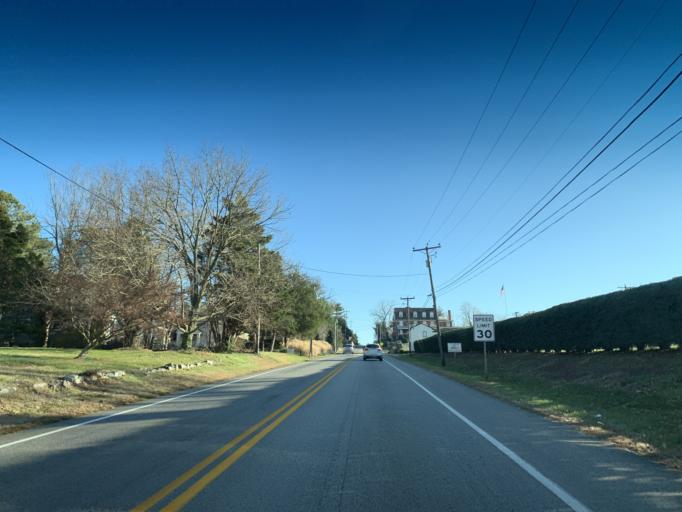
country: US
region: Delaware
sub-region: New Castle County
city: Middletown
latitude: 39.3627
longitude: -75.8810
